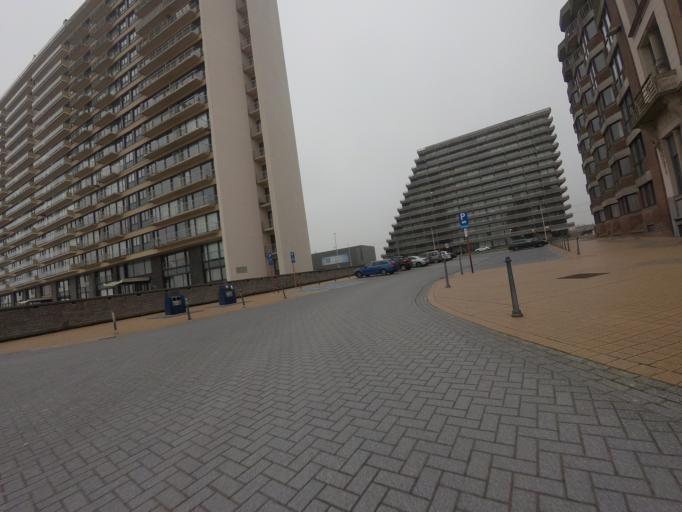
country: BE
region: Flanders
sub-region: Provincie West-Vlaanderen
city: Ostend
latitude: 51.2230
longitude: 2.8938
